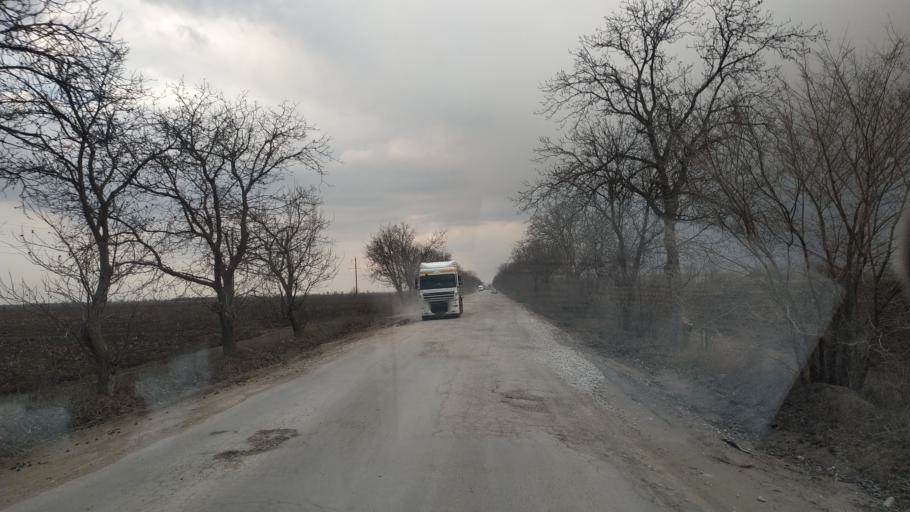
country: MD
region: Telenesti
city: Grigoriopol
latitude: 47.0482
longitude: 29.2935
